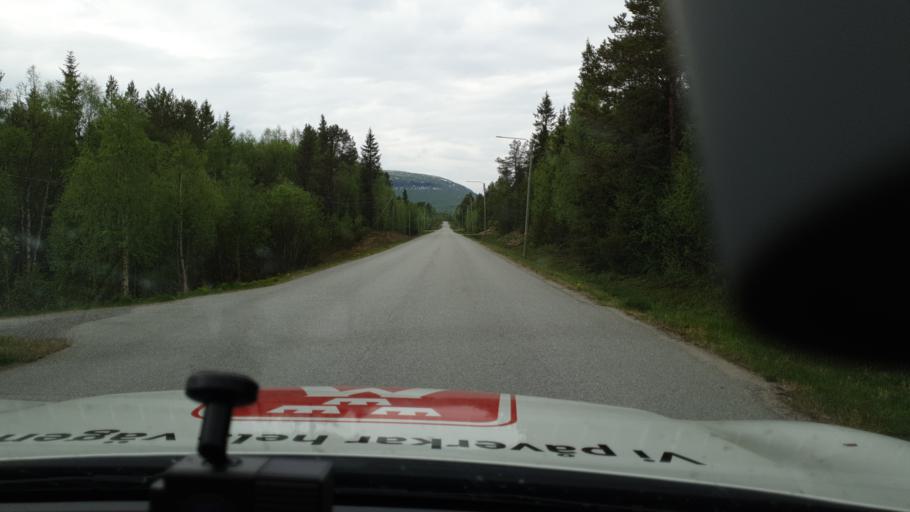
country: SE
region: Vaesterbotten
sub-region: Storumans Kommun
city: Fristad
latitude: 65.9572
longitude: 16.2007
